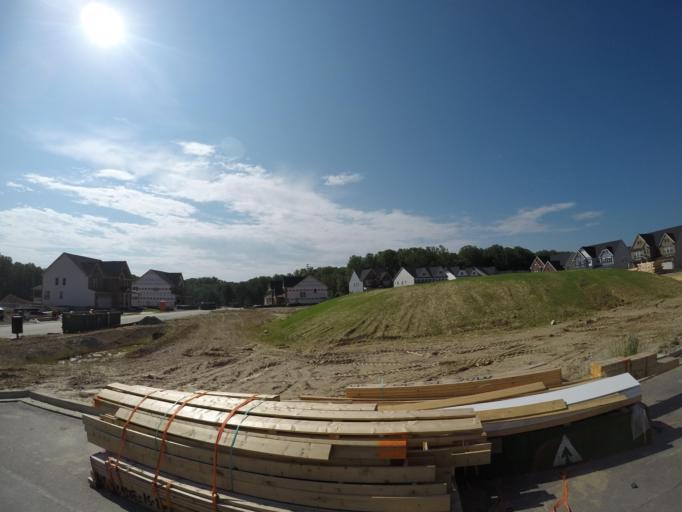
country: US
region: Maryland
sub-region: Howard County
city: Riverside
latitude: 39.1945
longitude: -76.9039
